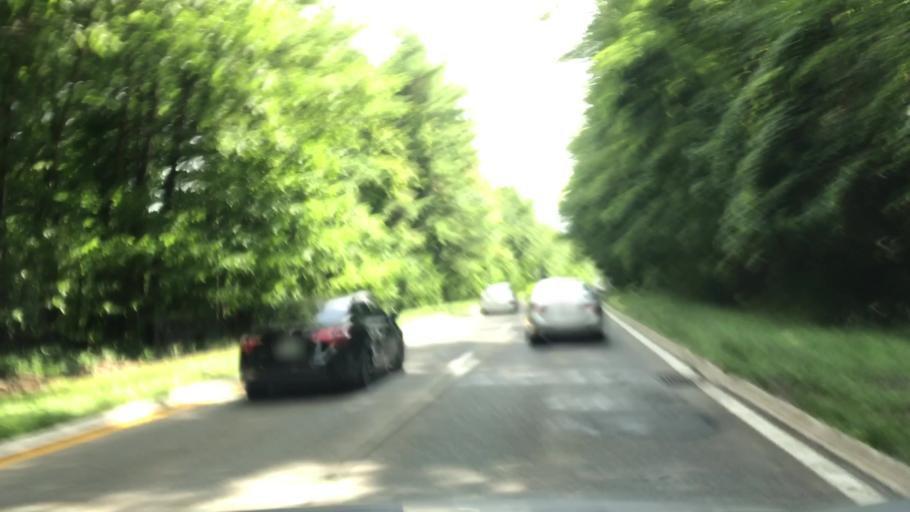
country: US
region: New York
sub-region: Rockland County
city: New Square
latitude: 41.1353
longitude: -74.0171
